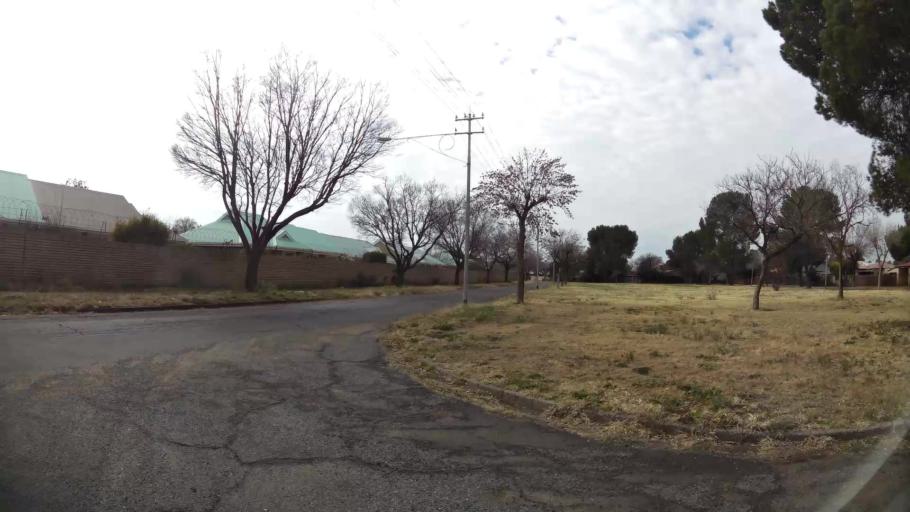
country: ZA
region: Orange Free State
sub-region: Mangaung Metropolitan Municipality
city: Bloemfontein
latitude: -29.1294
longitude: 26.1972
